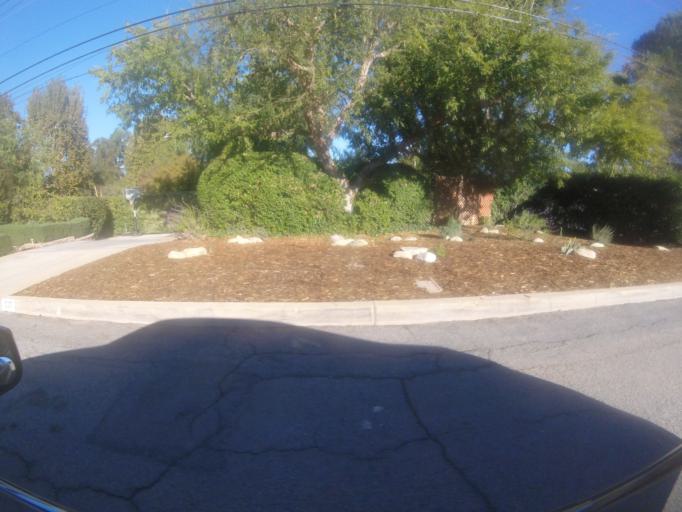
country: US
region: California
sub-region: San Bernardino County
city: Redlands
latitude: 34.0270
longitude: -117.1862
